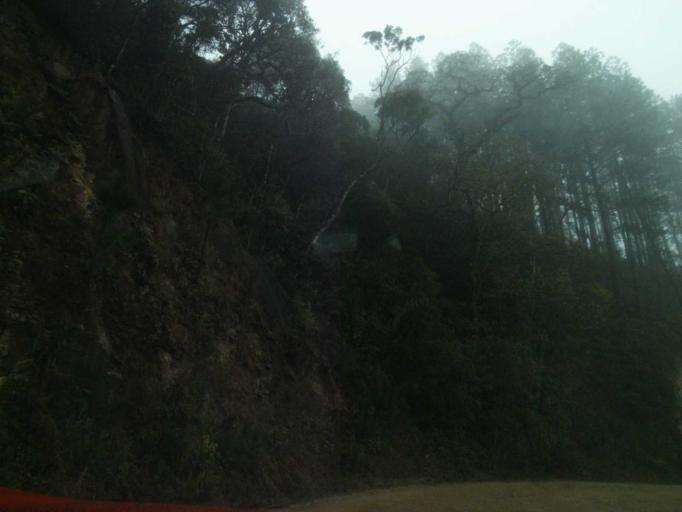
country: BR
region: Santa Catarina
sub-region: Anitapolis
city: Anitapolis
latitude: -27.9199
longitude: -49.1752
